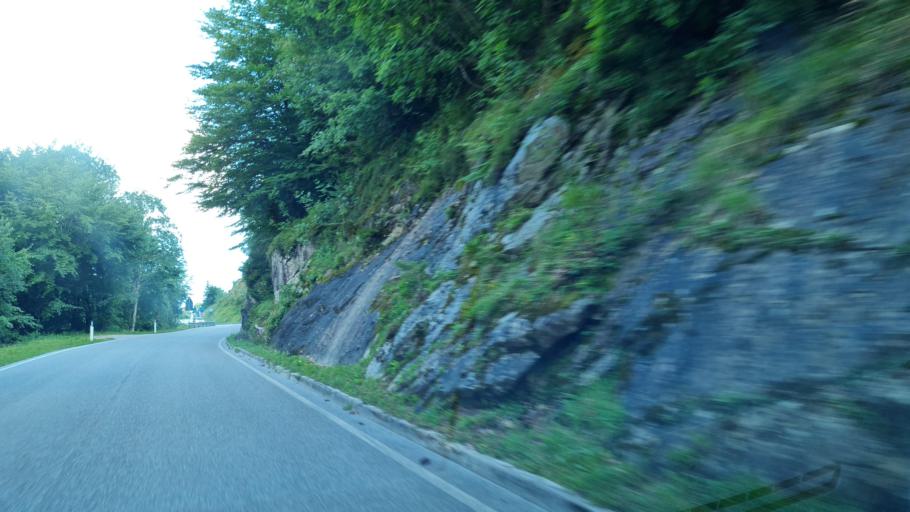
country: IT
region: Trentino-Alto Adige
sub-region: Provincia di Trento
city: Samone
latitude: 46.1073
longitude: 11.5001
